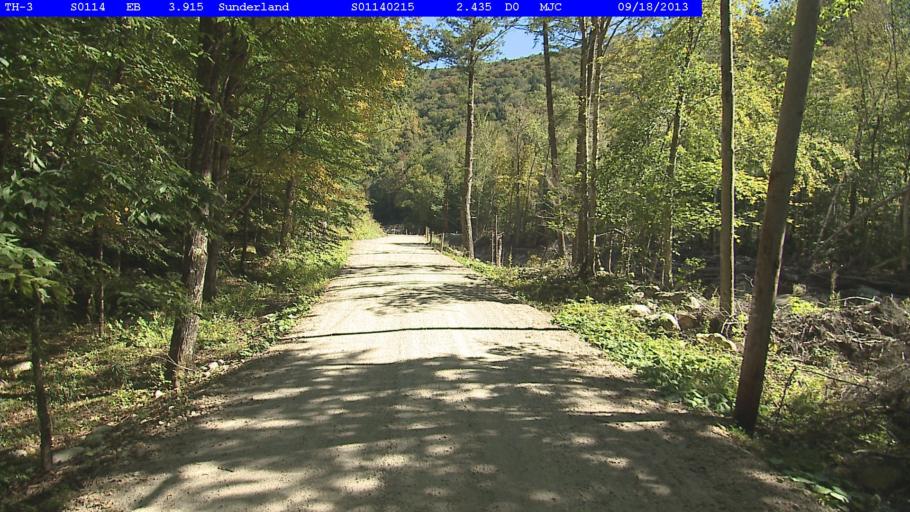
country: US
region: Vermont
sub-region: Bennington County
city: Arlington
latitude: 43.0400
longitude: -73.1101
